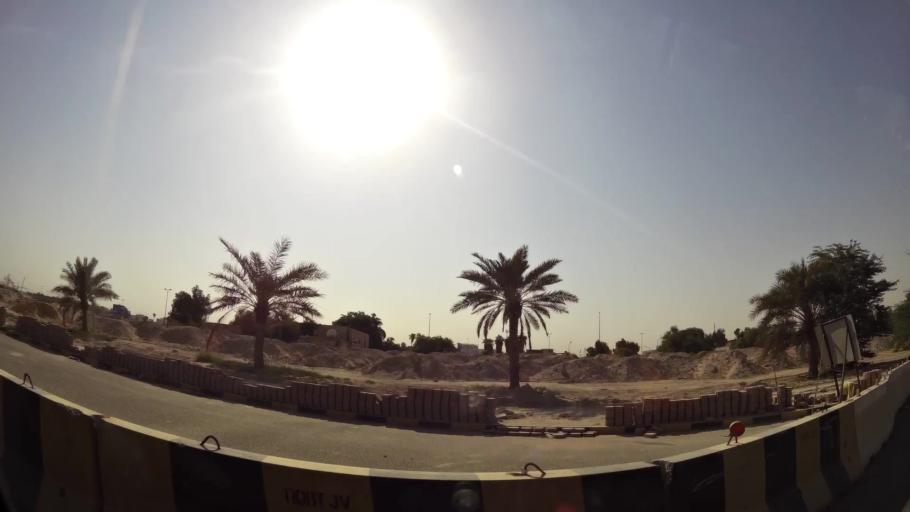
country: KW
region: Al Asimah
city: Ash Shamiyah
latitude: 29.3566
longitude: 47.9487
